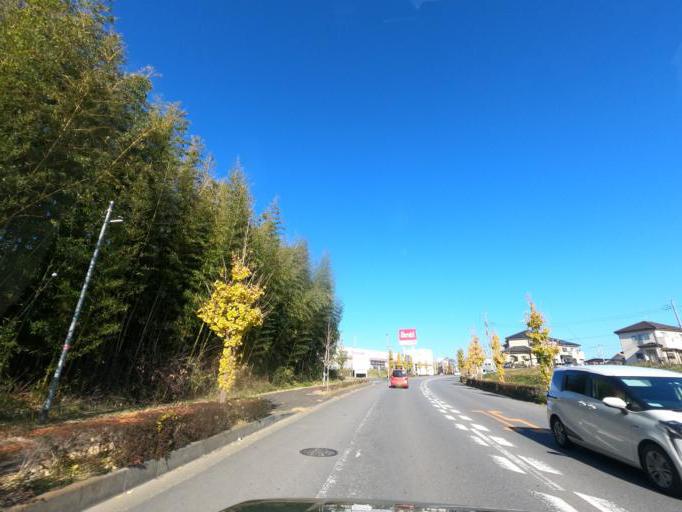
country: JP
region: Ibaraki
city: Mitsukaido
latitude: 35.9871
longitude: 139.9774
